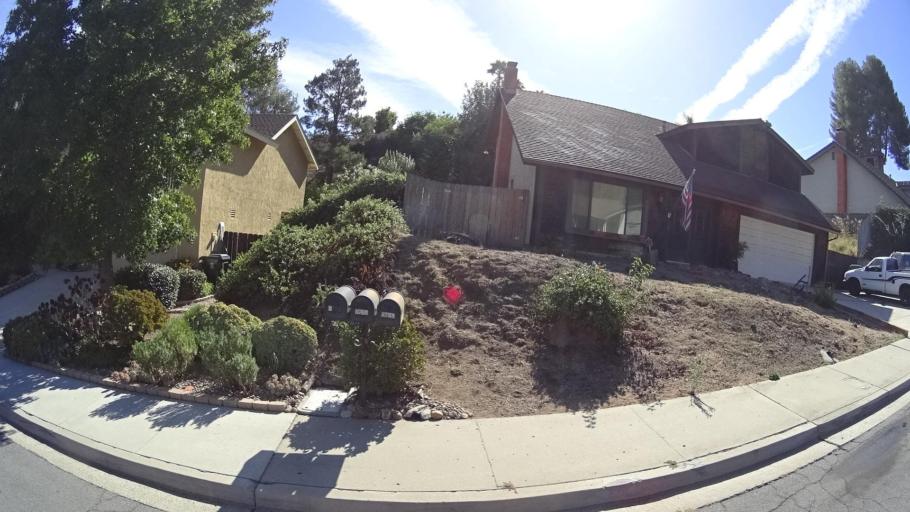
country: US
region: California
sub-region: San Diego County
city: Winter Gardens
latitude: 32.8368
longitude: -116.9186
